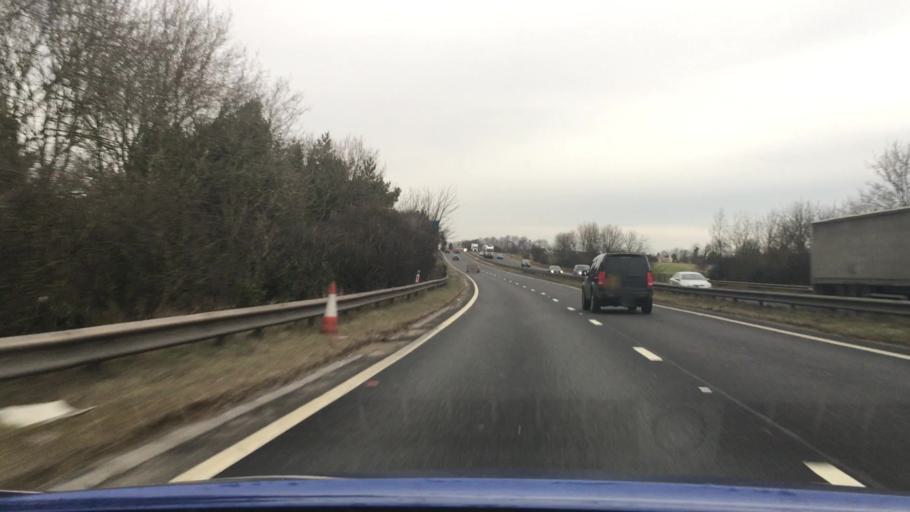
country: GB
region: England
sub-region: City and Borough of Wakefield
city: Darrington
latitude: 53.6725
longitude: -1.2609
